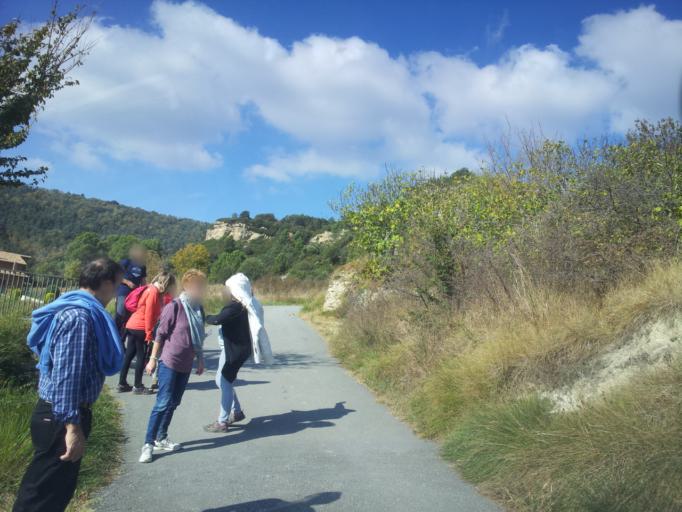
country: ES
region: Catalonia
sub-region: Provincia de Barcelona
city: Gurb
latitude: 41.9464
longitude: 2.2120
